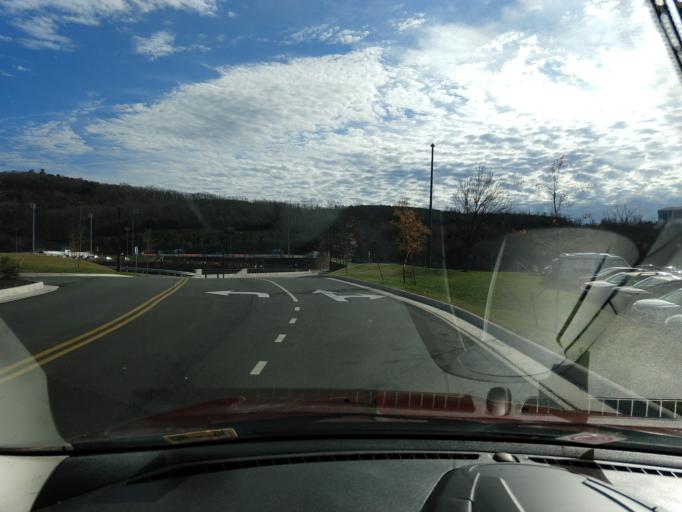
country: US
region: Virginia
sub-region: City of Lynchburg
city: West Lynchburg
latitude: 37.3441
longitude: -79.1843
